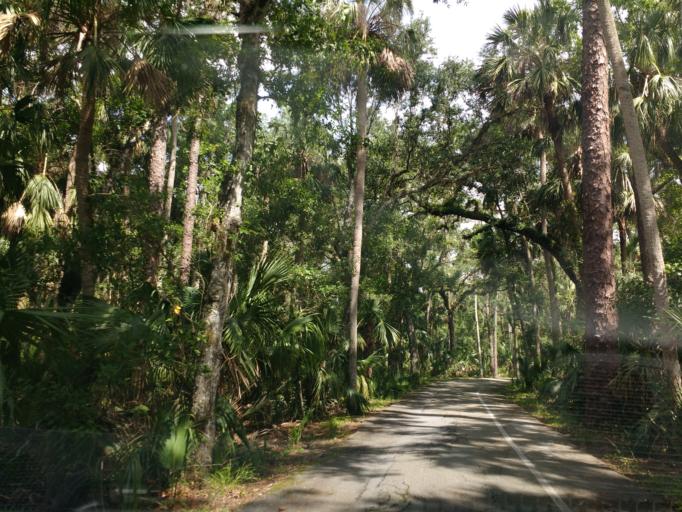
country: US
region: Florida
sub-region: Highlands County
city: Sebring
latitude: 27.4718
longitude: -81.5492
